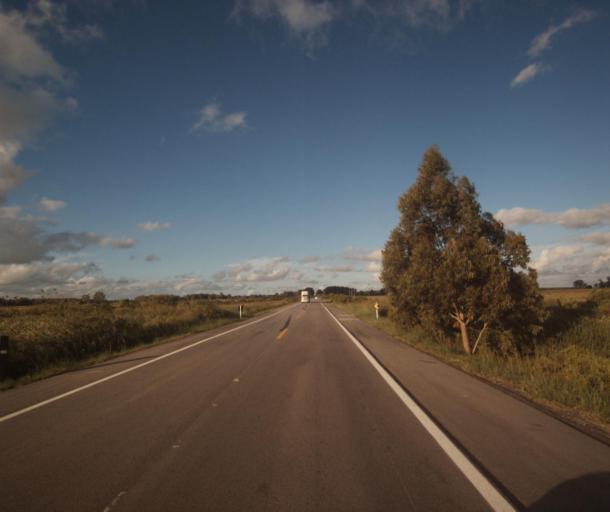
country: BR
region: Rio Grande do Sul
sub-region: Rio Grande
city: Rio Grande
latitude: -32.1310
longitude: -52.3705
